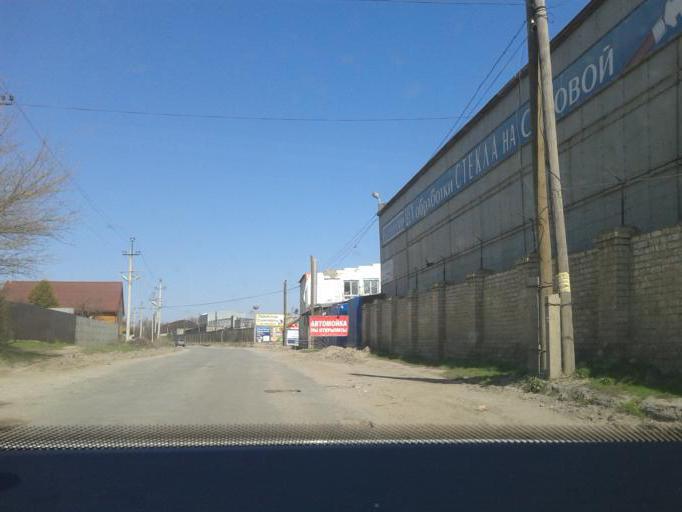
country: RU
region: Volgograd
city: Volgograd
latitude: 48.6802
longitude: 44.4620
